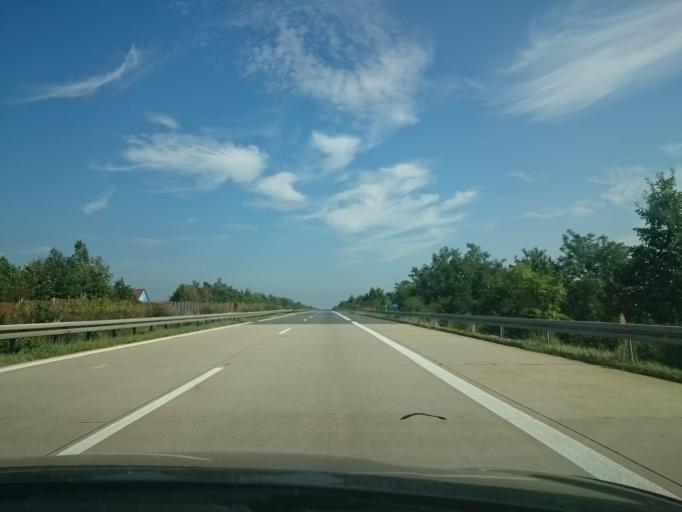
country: DE
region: Brandenburg
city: Schwarzheide
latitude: 51.4715
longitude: 13.8666
